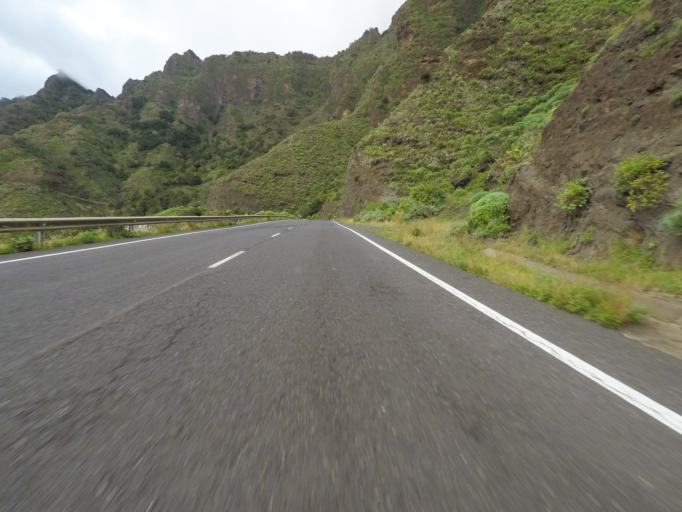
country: ES
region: Canary Islands
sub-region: Provincia de Santa Cruz de Tenerife
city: Hermigua
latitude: 28.1319
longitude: -17.1789
